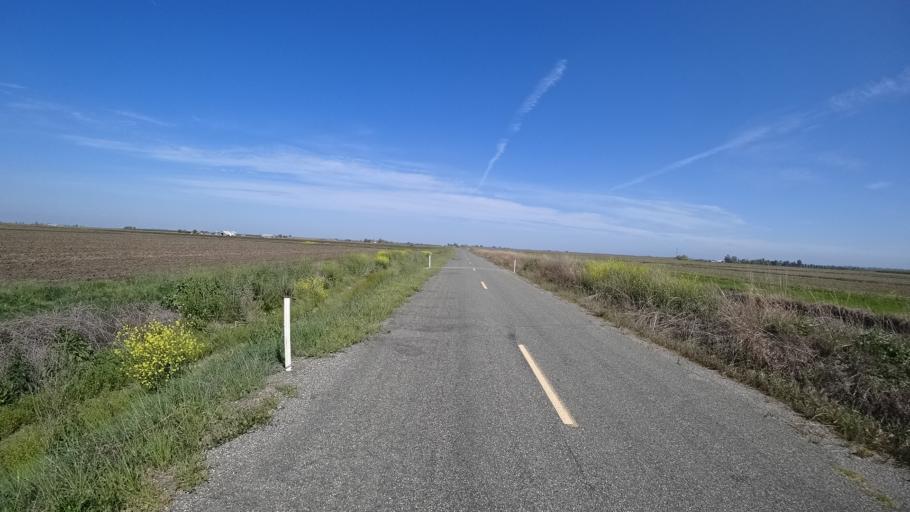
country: US
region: California
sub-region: Glenn County
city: Hamilton City
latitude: 39.5963
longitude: -122.0274
